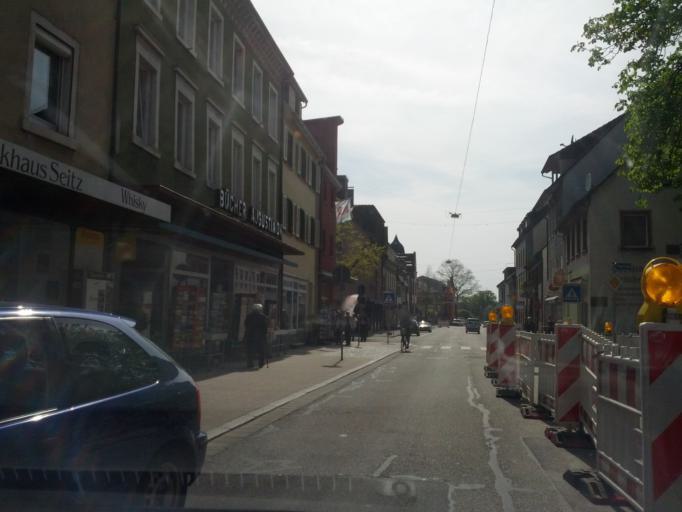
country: DE
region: Baden-Wuerttemberg
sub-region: Freiburg Region
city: Waldkirch
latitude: 48.0934
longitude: 7.9602
